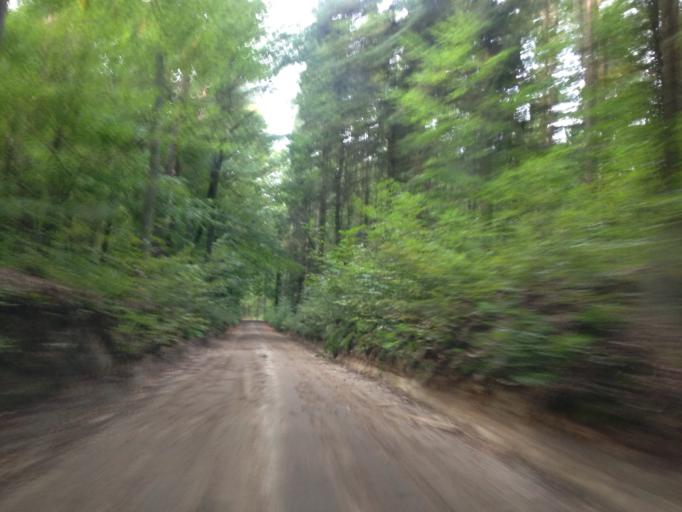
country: PL
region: Warmian-Masurian Voivodeship
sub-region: Powiat ilawski
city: Susz
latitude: 53.7566
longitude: 19.3074
